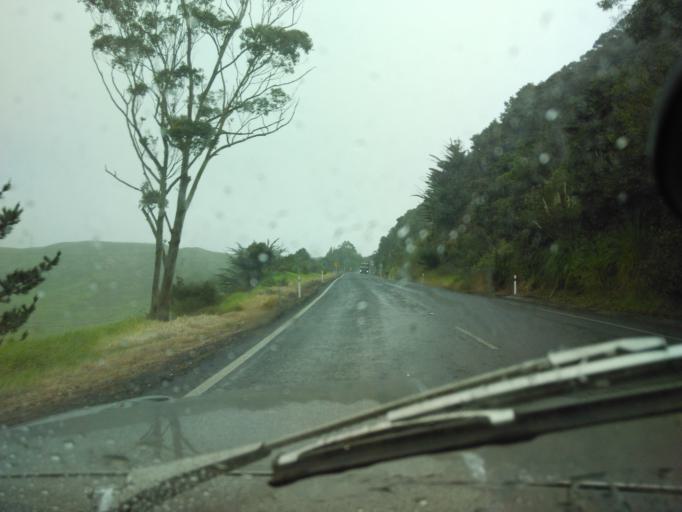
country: NZ
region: Auckland
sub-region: Auckland
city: Wellsford
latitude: -36.4332
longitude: 174.4353
